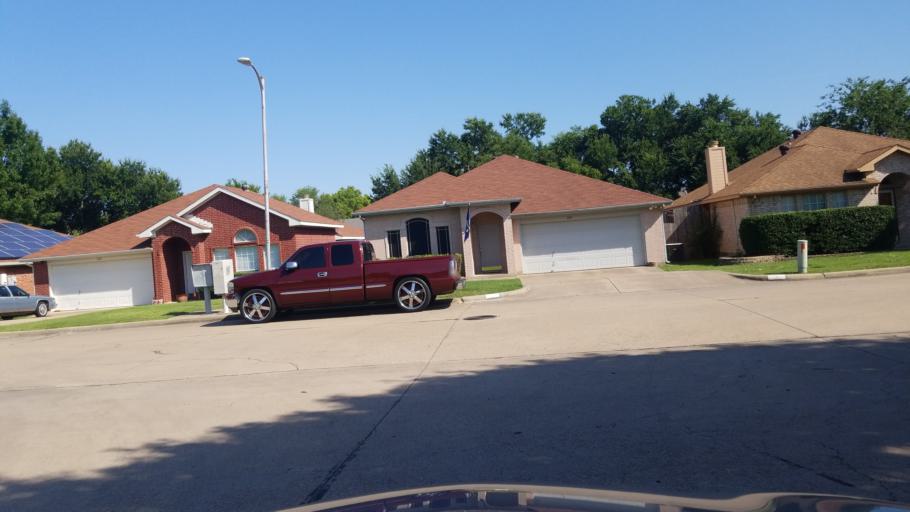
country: US
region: Texas
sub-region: Dallas County
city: Grand Prairie
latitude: 32.6895
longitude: -97.0129
